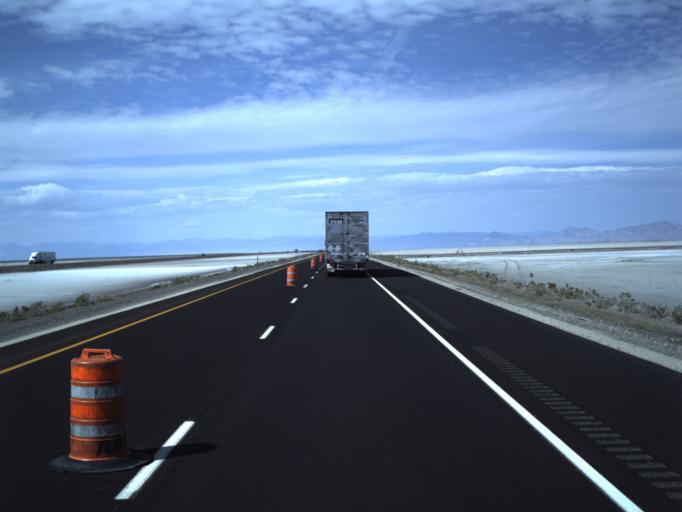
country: US
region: Utah
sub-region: Tooele County
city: Wendover
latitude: 40.7334
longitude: -113.5709
